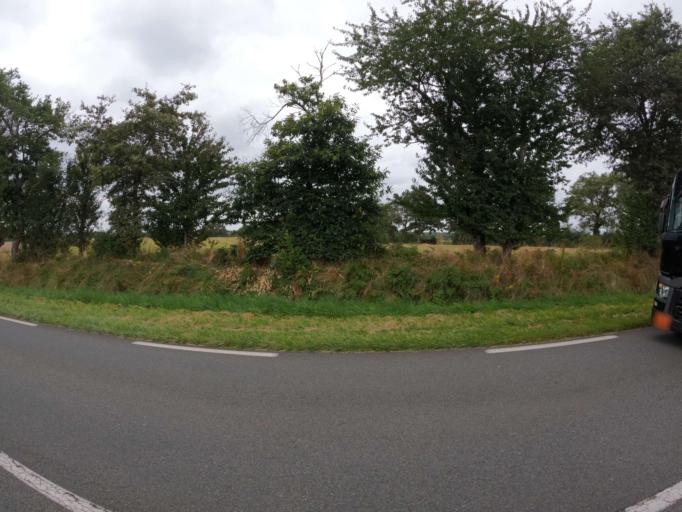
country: FR
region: Poitou-Charentes
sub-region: Departement de la Charente
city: Confolens
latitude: 46.0566
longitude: 0.6103
